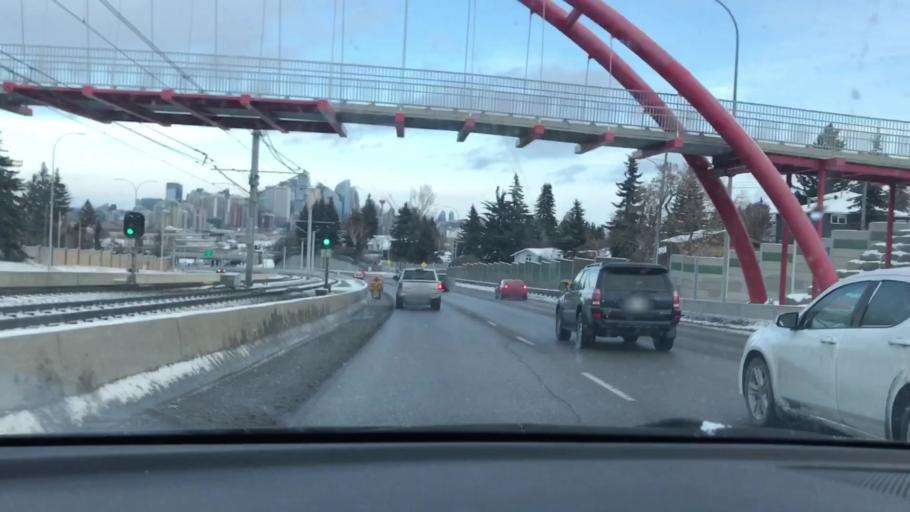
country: CA
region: Alberta
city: Calgary
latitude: 51.0415
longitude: -114.1196
